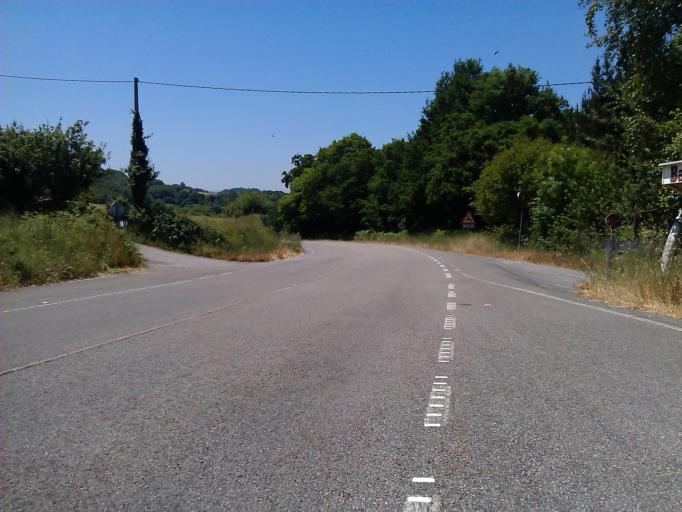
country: ES
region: Galicia
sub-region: Provincia de Lugo
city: Samos
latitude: 42.7382
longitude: -7.3086
